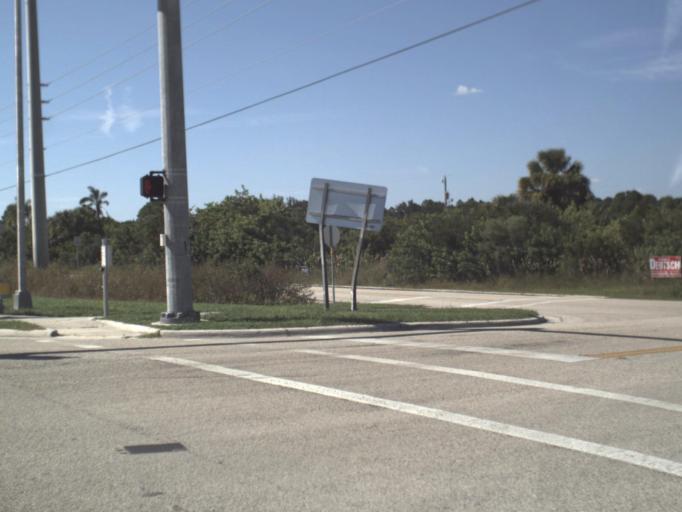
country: US
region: Florida
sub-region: Charlotte County
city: Rotonda
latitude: 26.9329
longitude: -82.2719
